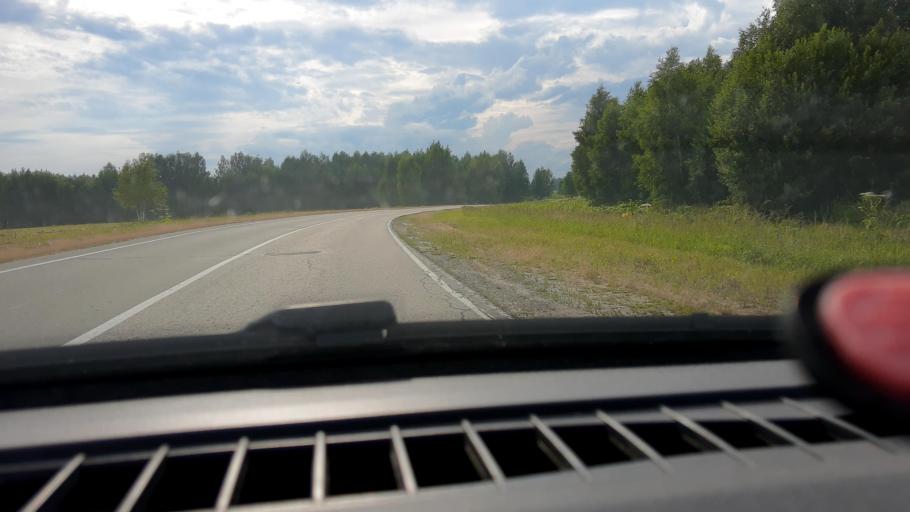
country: RU
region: Nizjnij Novgorod
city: Sitniki
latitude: 56.4955
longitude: 44.0091
